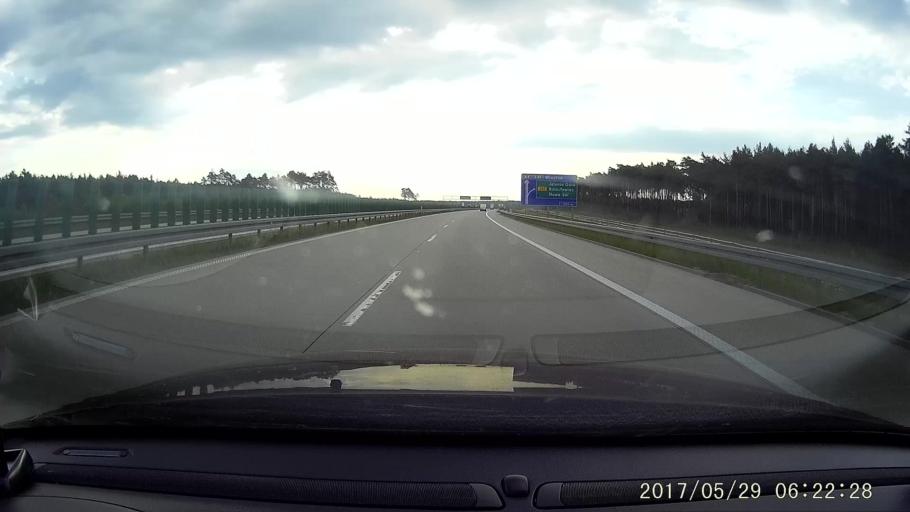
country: PL
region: Lower Silesian Voivodeship
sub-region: Powiat lubanski
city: Pisarzowice
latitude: 51.2146
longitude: 15.2077
